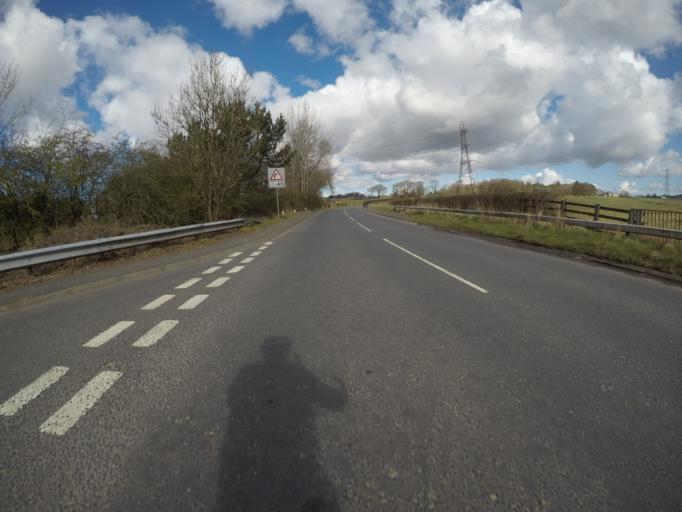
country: GB
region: Scotland
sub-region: North Ayrshire
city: Beith
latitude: 55.7398
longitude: -4.6250
